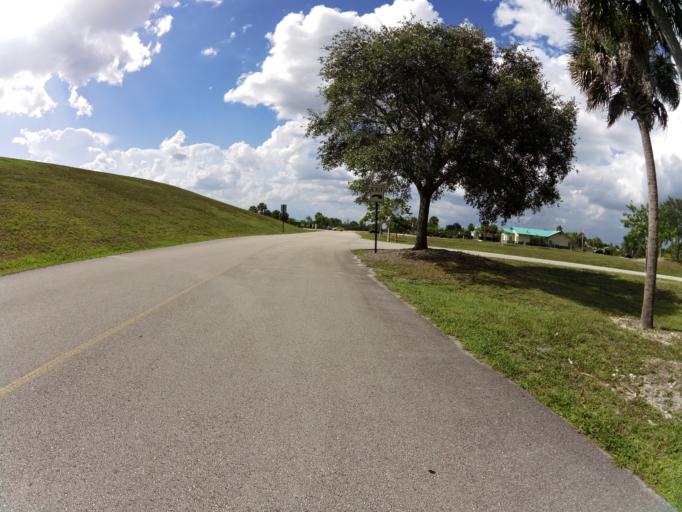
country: US
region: Florida
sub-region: Broward County
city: Southwest Ranches
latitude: 26.0671
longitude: -80.3397
